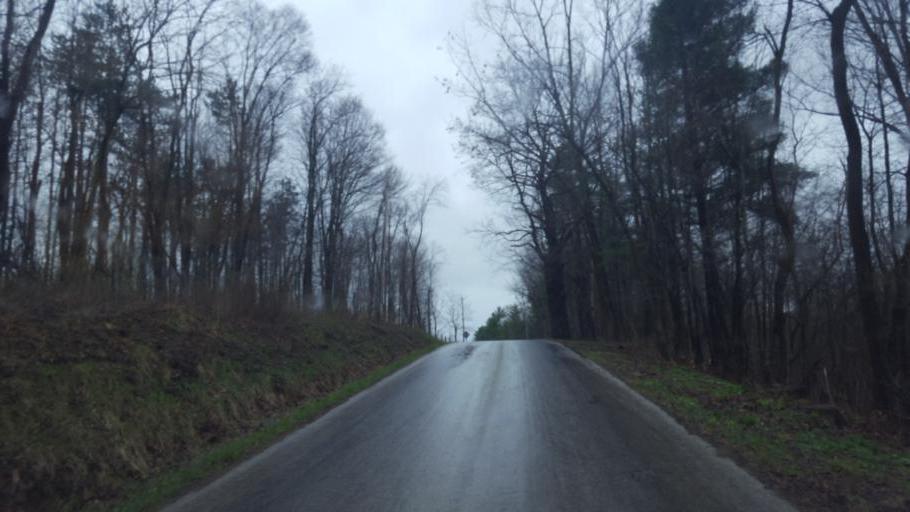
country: US
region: Ohio
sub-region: Knox County
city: Fredericktown
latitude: 40.5561
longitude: -82.6040
